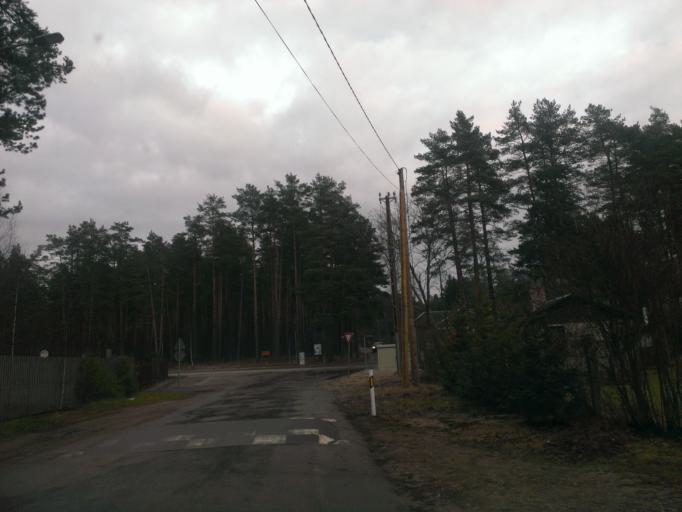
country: LV
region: Riga
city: Bergi
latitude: 57.0096
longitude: 24.3257
